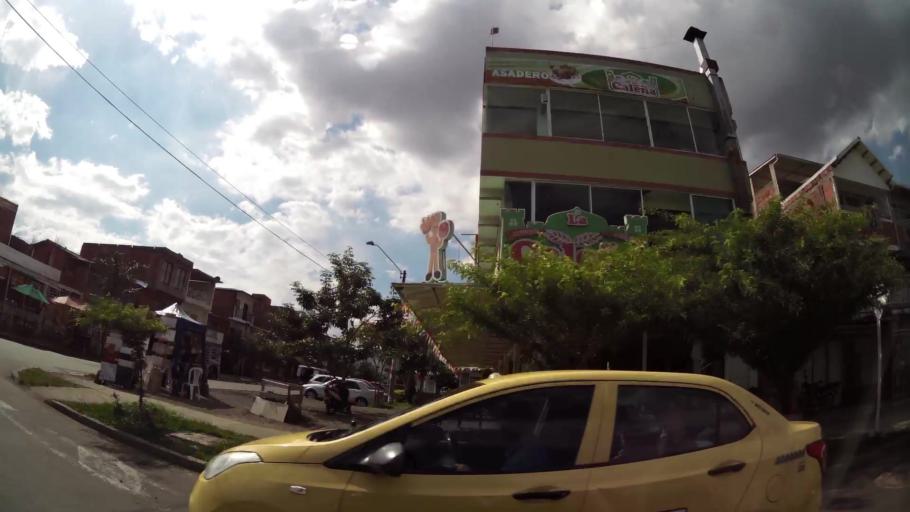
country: CO
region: Valle del Cauca
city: Cali
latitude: 3.3947
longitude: -76.5092
